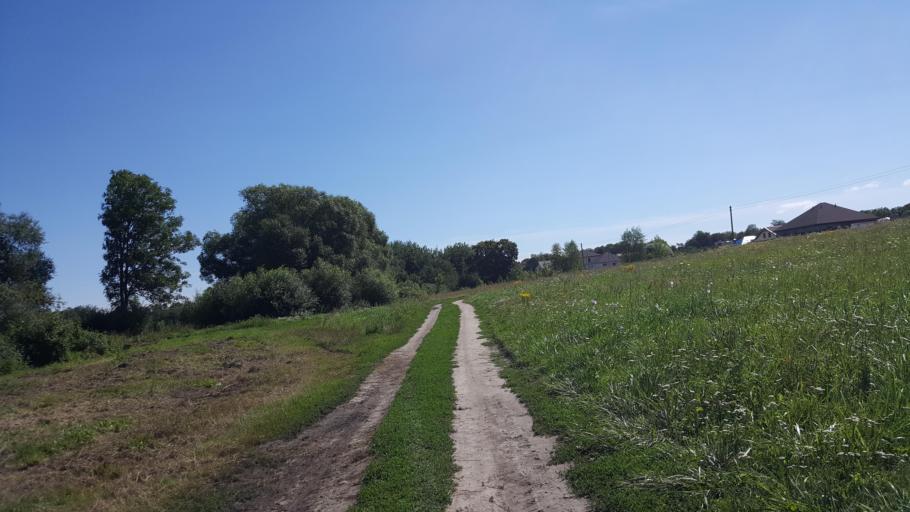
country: BY
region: Brest
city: Charnawchytsy
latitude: 52.2710
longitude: 23.7615
